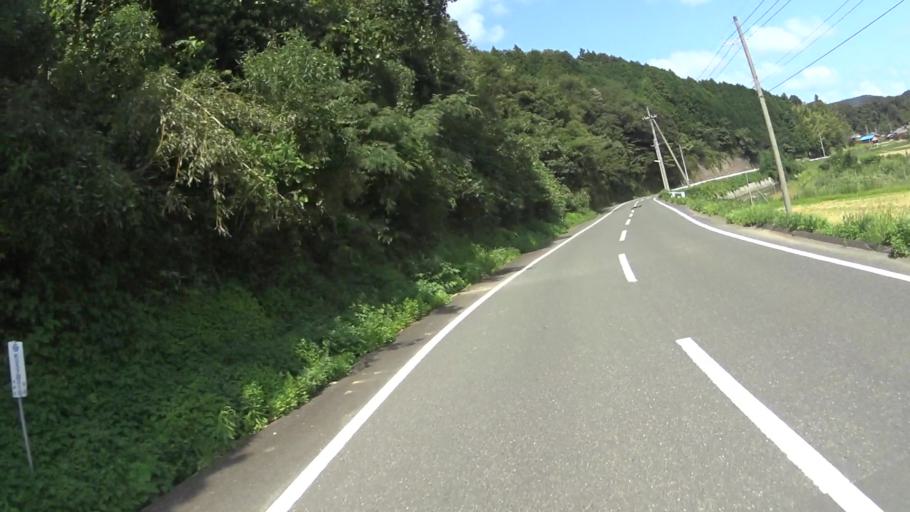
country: JP
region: Kyoto
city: Miyazu
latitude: 35.7113
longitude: 135.2501
